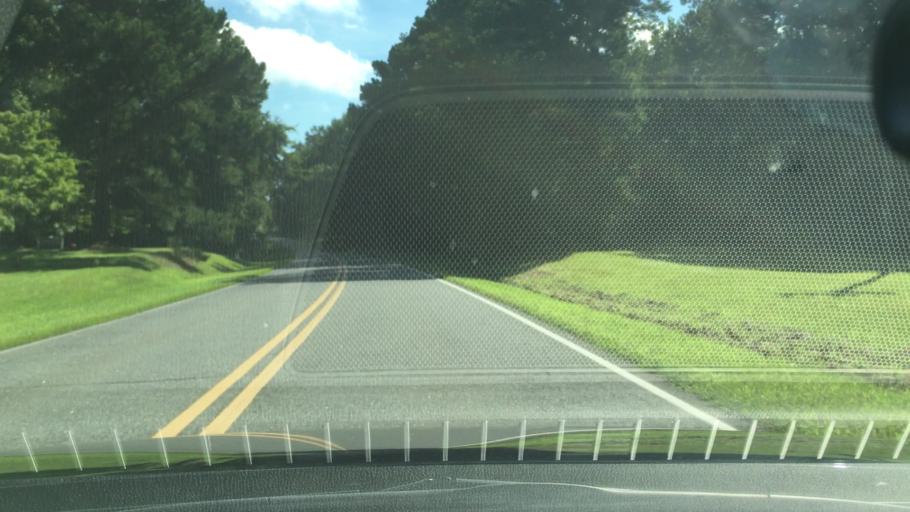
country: US
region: Georgia
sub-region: Putnam County
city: Jefferson
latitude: 33.4501
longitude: -83.3083
